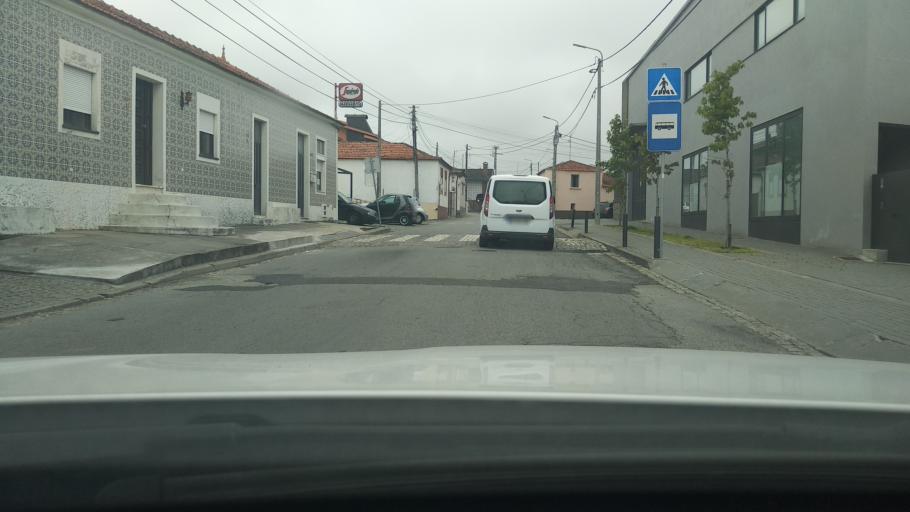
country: PT
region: Aveiro
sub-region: Espinho
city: Souto
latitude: 40.9861
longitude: -8.6199
